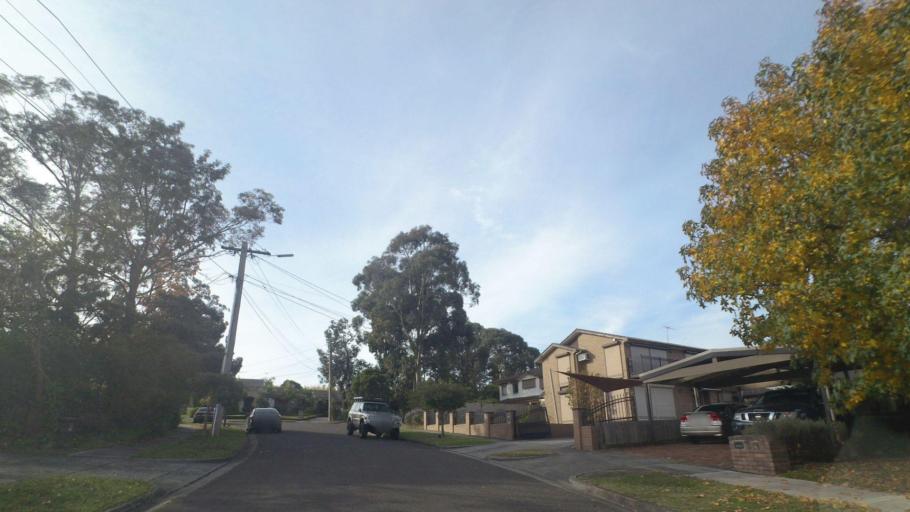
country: AU
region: Victoria
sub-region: Manningham
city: Doncaster East
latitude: -37.7777
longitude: 145.1557
